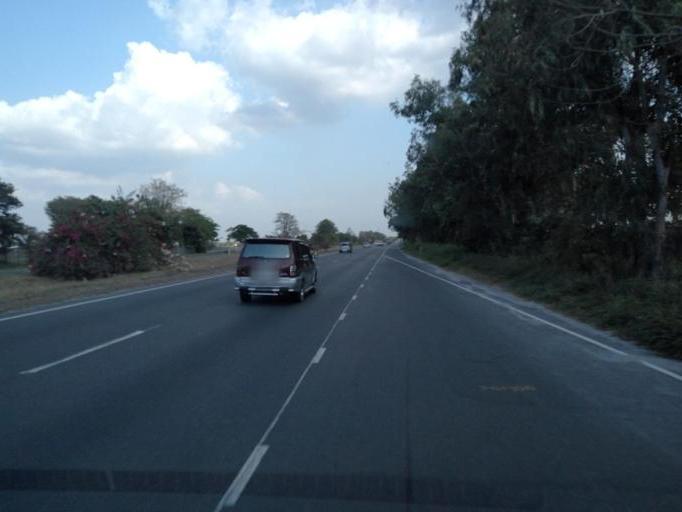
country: PH
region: Central Luzon
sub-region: Province of Pampanga
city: Acli
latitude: 15.1282
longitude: 120.6455
